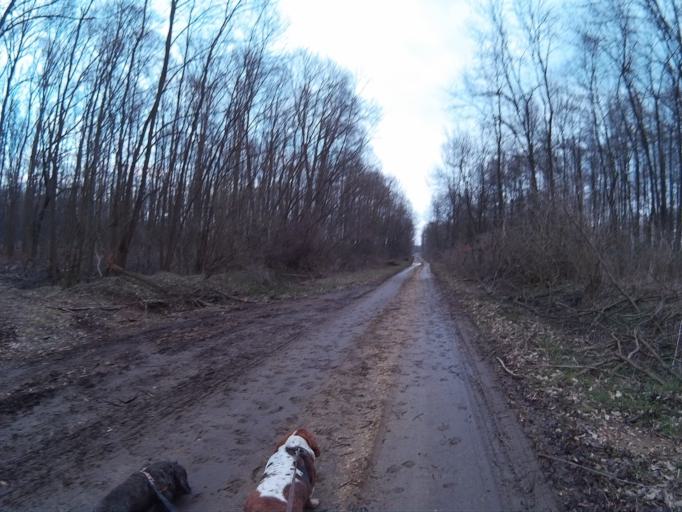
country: HU
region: Vas
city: Janoshaza
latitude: 47.1252
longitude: 17.0366
